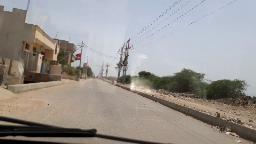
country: PK
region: Sindh
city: Malir Cantonment
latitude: 24.8352
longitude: 67.2055
